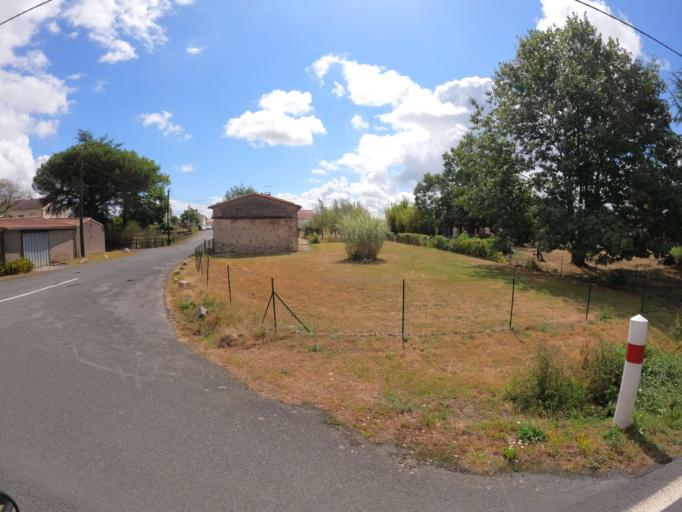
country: FR
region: Pays de la Loire
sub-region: Departement de la Loire-Atlantique
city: Vallet
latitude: 47.1833
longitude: -1.2568
